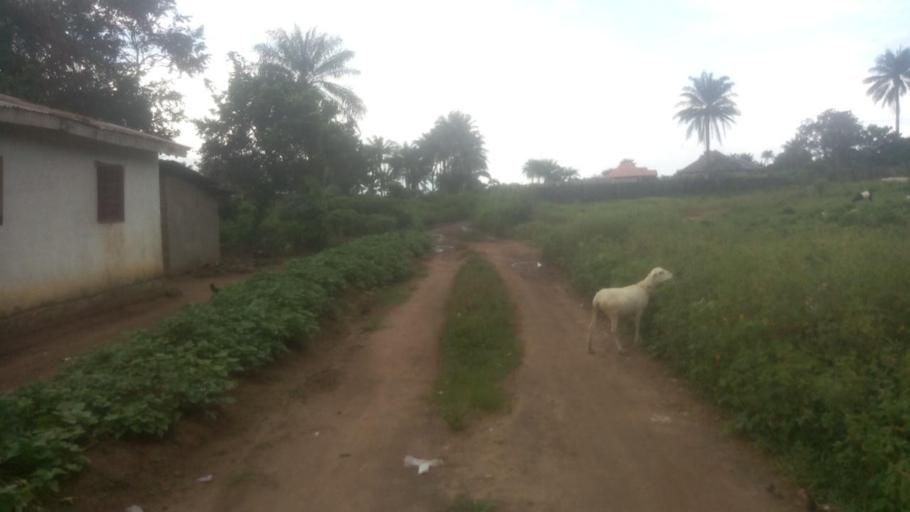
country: SL
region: Northern Province
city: Masoyila
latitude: 8.5738
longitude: -13.1654
